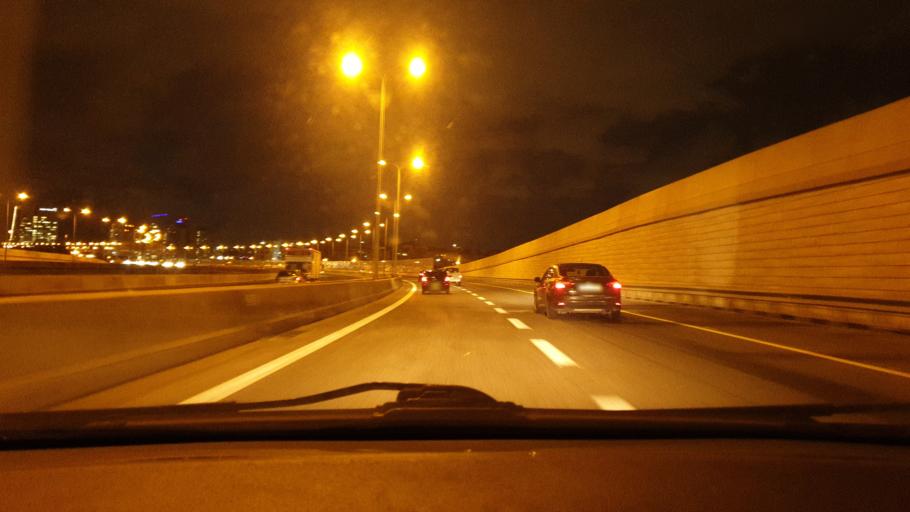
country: IL
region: Central District
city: Ness Ziona
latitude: 31.9433
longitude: 34.8150
